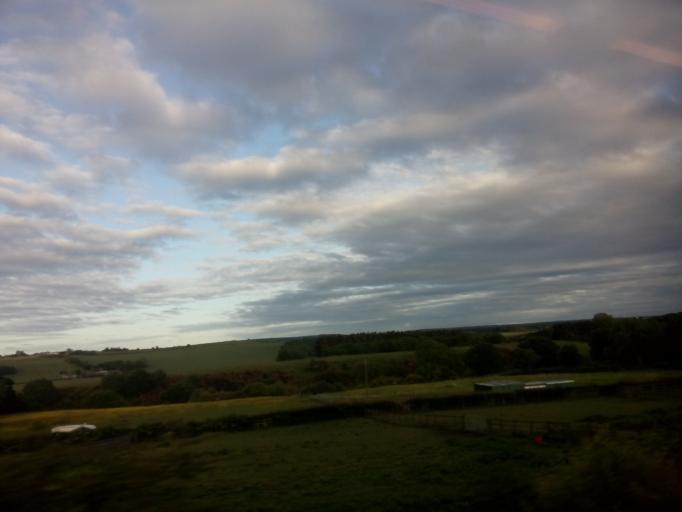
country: GB
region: England
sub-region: County Durham
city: Chester-le-Street
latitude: 54.8403
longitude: -1.5794
